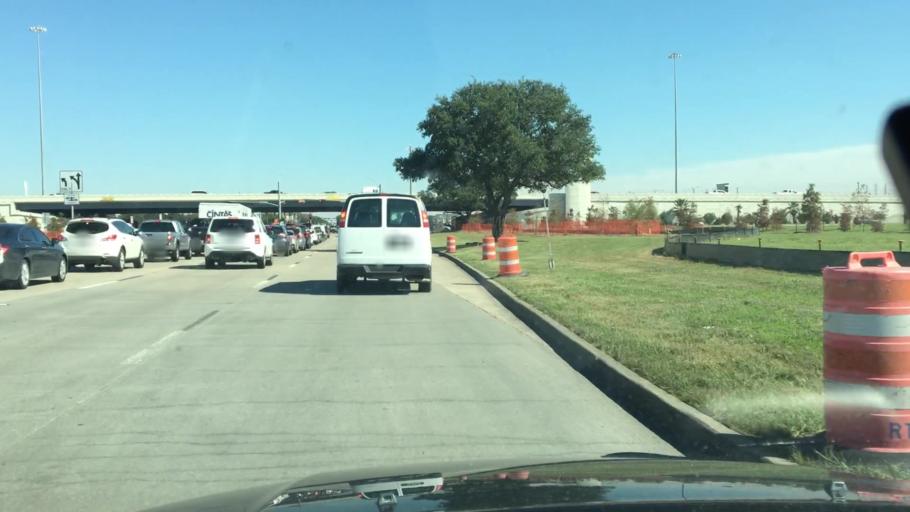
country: US
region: Texas
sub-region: Harris County
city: Webster
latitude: 29.5274
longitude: -95.1323
